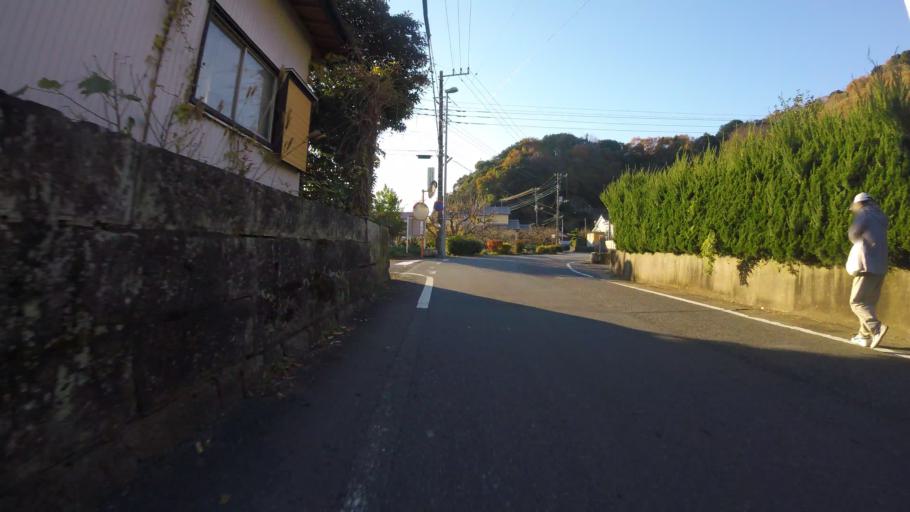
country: JP
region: Shizuoka
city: Mishima
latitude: 35.0265
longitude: 138.9376
